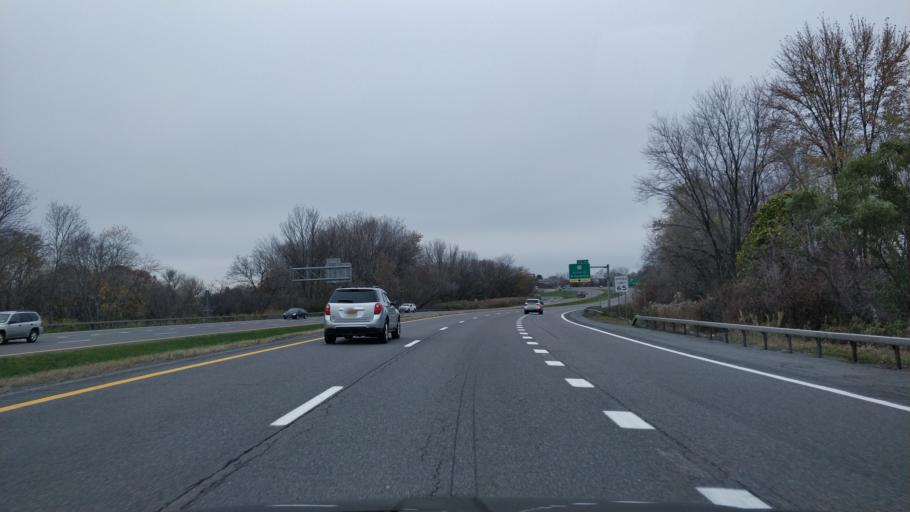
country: US
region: New York
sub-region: Onondaga County
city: North Syracuse
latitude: 43.1429
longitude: -76.1189
